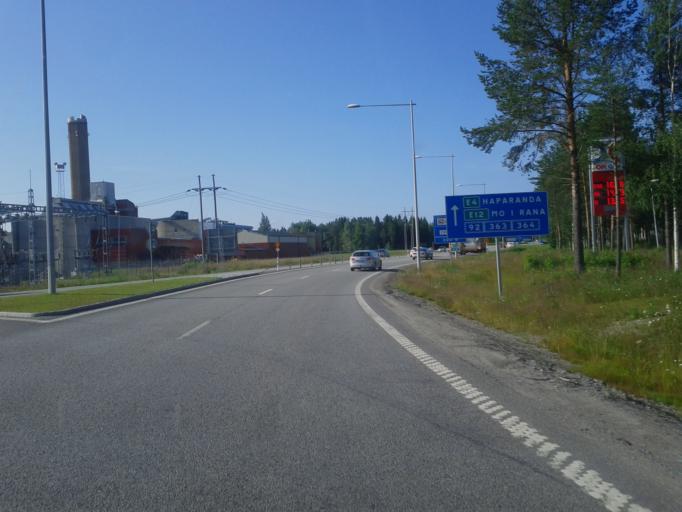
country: SE
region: Vaesterbotten
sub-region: Umea Kommun
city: Umea
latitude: 63.8104
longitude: 20.3263
